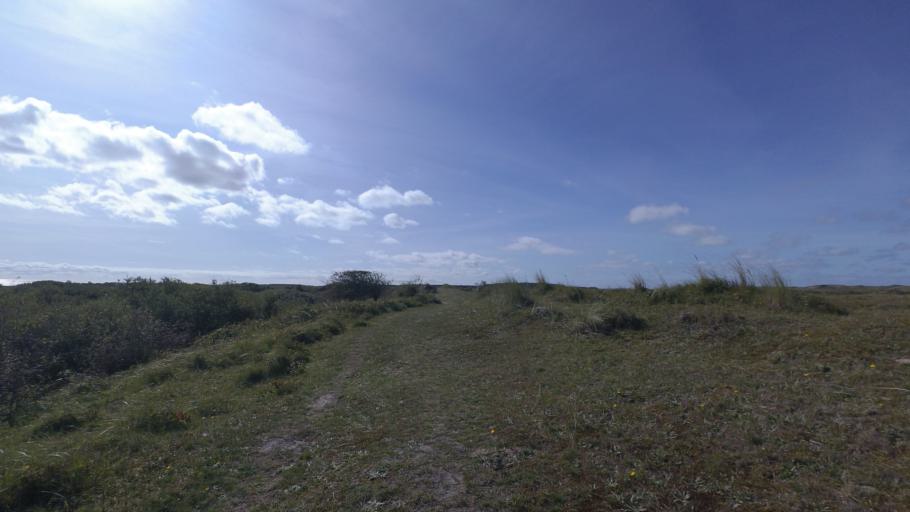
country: NL
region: Friesland
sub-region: Gemeente Ameland
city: Nes
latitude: 53.4539
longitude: 5.7328
